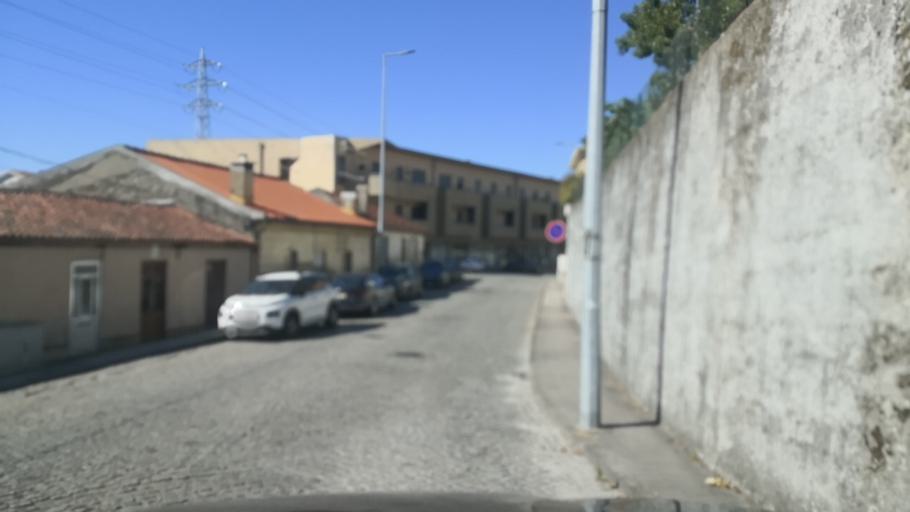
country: PT
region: Porto
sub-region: Santo Tirso
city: Santo Tirso
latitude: 41.3444
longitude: -8.4844
